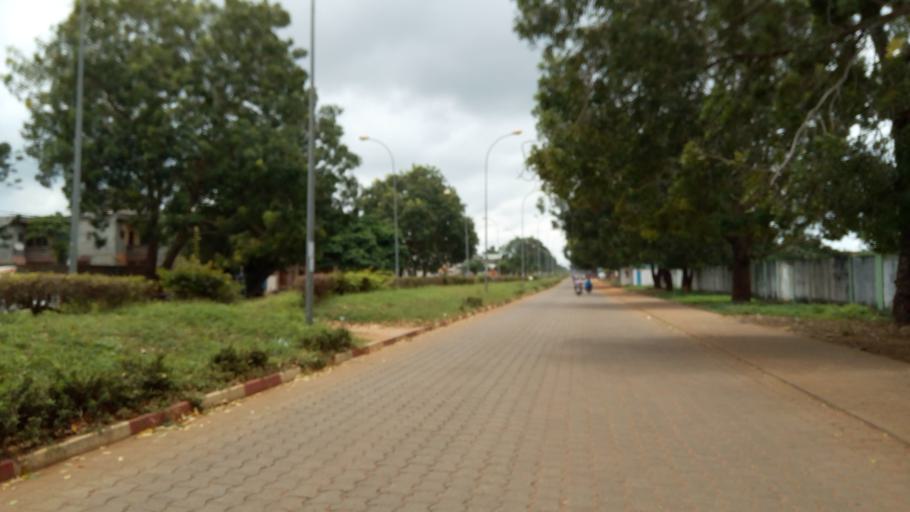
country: BJ
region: Queme
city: Porto-Novo
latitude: 6.4785
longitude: 2.6348
